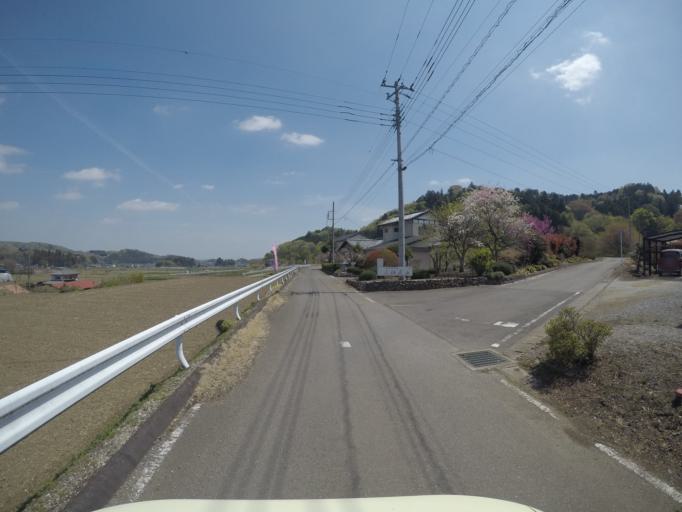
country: JP
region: Tochigi
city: Tochigi
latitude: 36.4517
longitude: 139.6964
